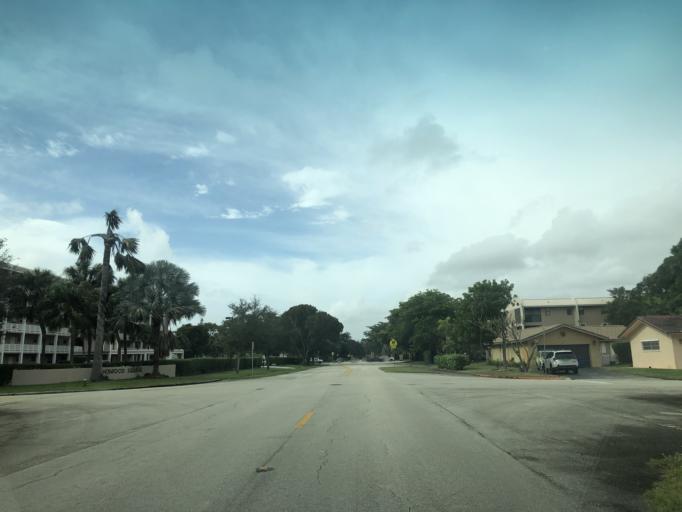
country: US
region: Florida
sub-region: Broward County
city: North Lauderdale
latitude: 26.2463
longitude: -80.2408
